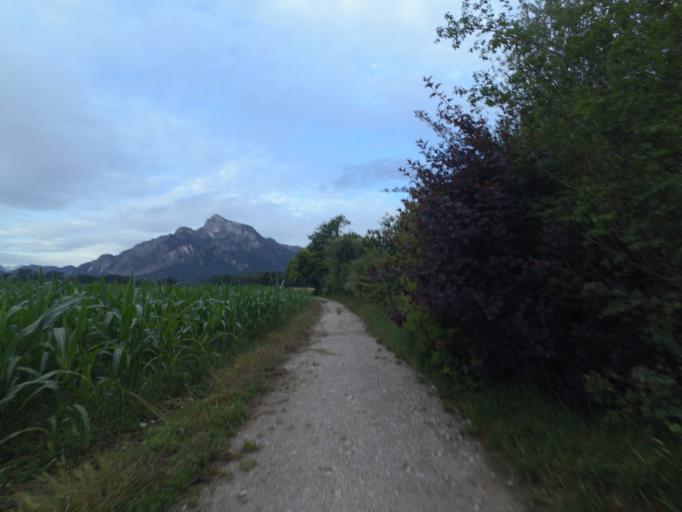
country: AT
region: Salzburg
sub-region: Politischer Bezirk Salzburg-Umgebung
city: Anif
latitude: 47.7651
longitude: 13.0546
